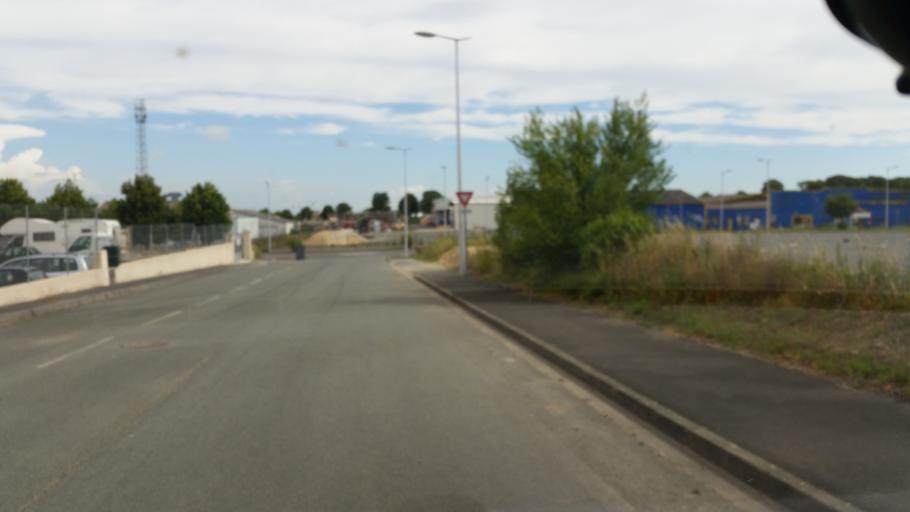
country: FR
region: Poitou-Charentes
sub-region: Departement de la Charente-Maritime
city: Surgeres
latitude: 46.1111
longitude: -0.7748
